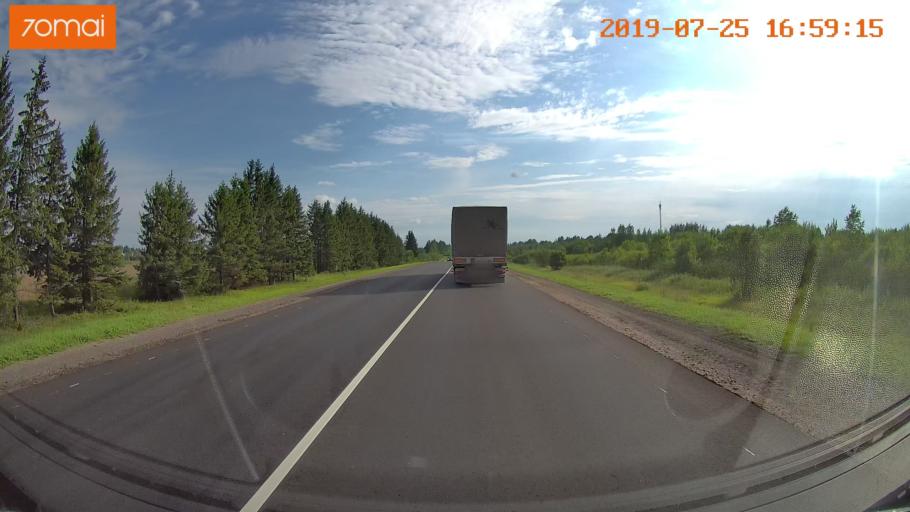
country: RU
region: Ivanovo
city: Furmanov
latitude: 57.2455
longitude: 41.1523
